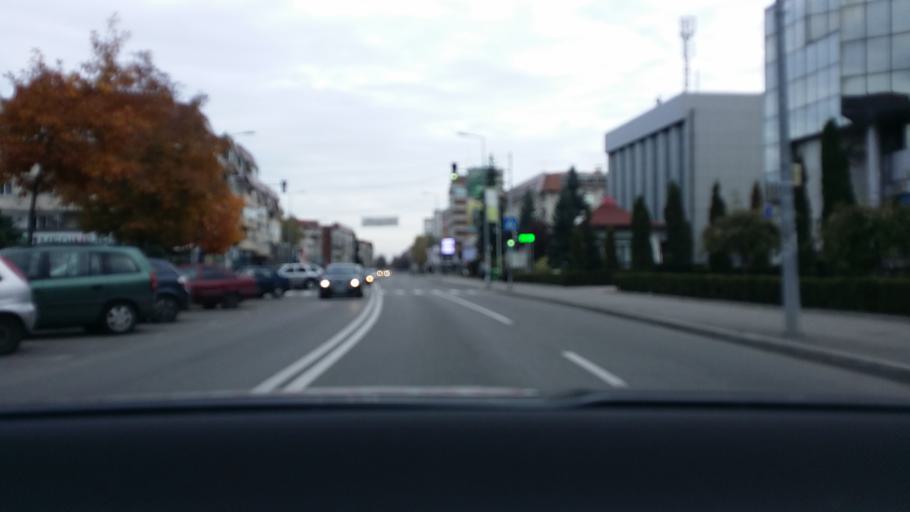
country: RO
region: Prahova
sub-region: Municipiul Campina
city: Campina
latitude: 45.1248
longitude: 25.7342
